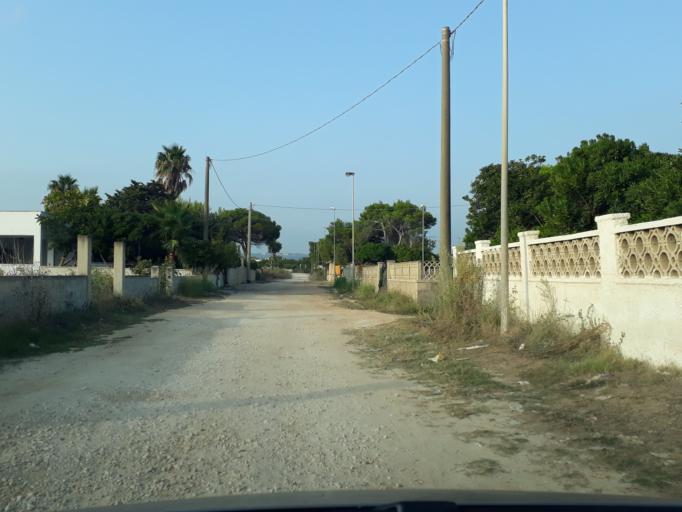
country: IT
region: Apulia
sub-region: Provincia di Brindisi
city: Carovigno
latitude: 40.7510
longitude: 17.7185
